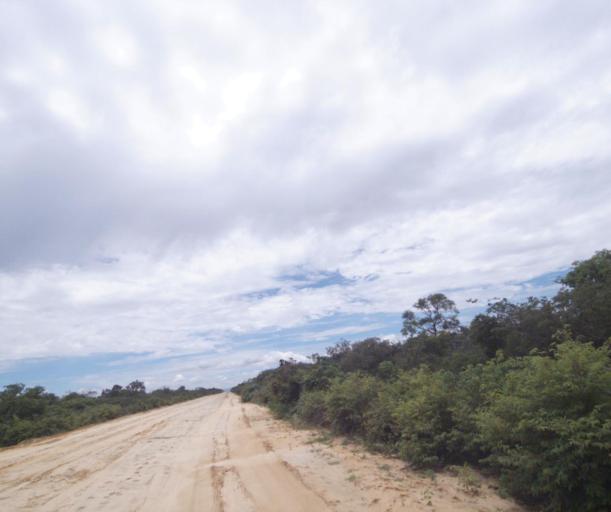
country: BR
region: Bahia
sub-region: Carinhanha
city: Carinhanha
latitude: -14.2609
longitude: -43.8217
